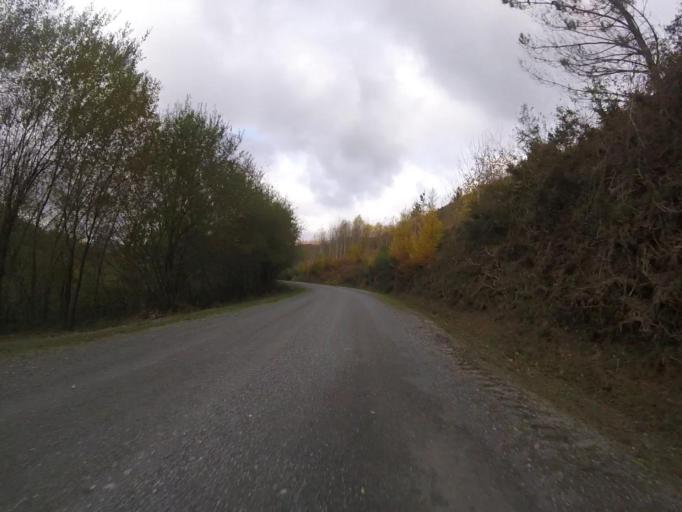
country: ES
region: Navarre
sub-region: Provincia de Navarra
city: Goizueta
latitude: 43.2199
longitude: -1.8321
